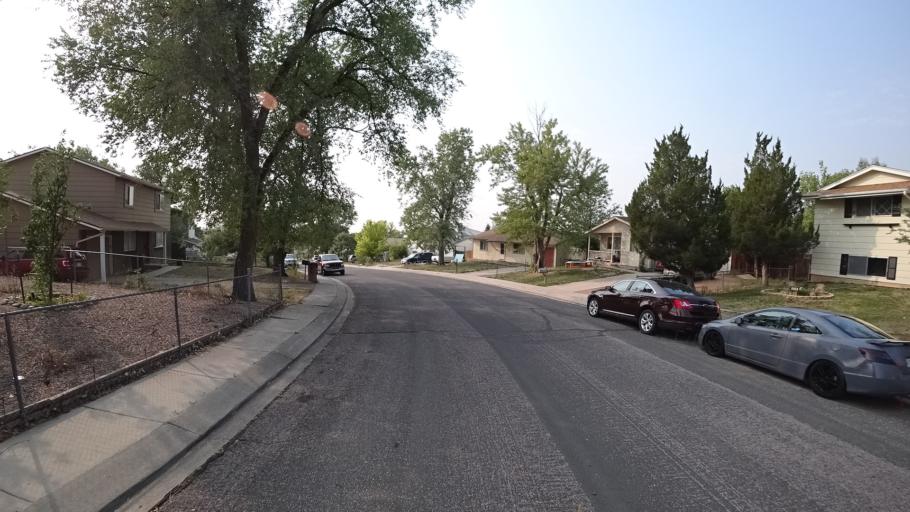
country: US
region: Colorado
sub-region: El Paso County
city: Stratmoor
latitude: 38.8019
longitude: -104.7647
